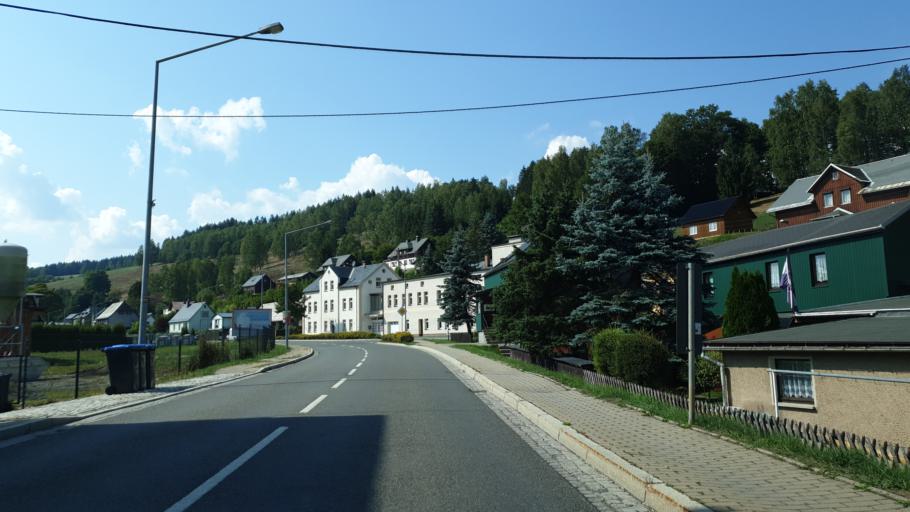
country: DE
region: Saxony
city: Klingenthal
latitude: 50.3563
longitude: 12.4462
